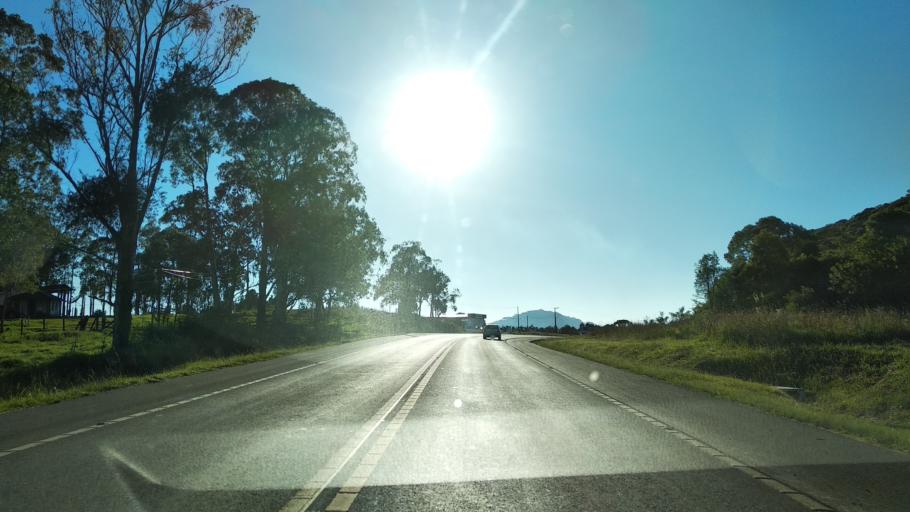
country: BR
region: Santa Catarina
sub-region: Lages
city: Lages
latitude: -27.7929
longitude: -50.3755
